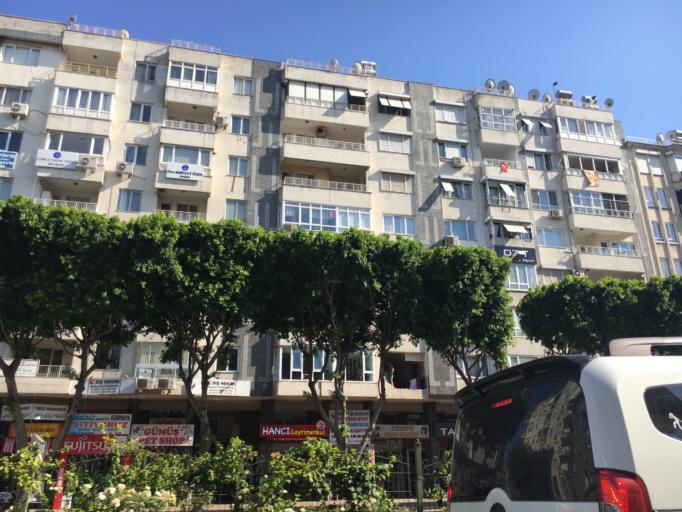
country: TR
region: Antalya
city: Antalya
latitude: 36.8905
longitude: 30.6917
